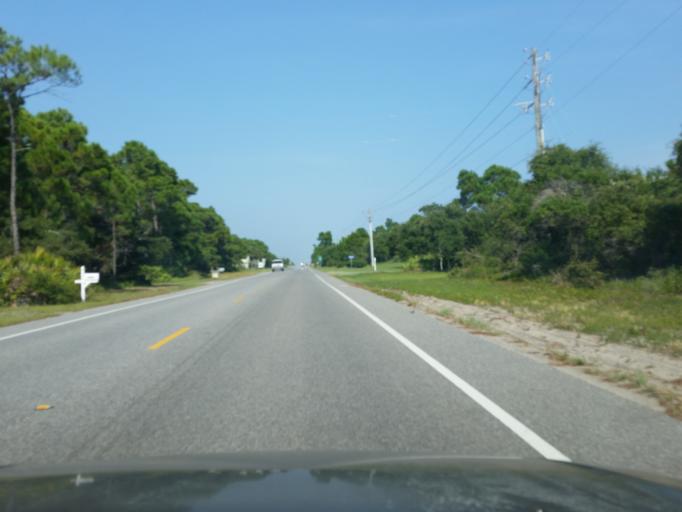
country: US
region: Alabama
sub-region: Mobile County
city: Dauphin Island
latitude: 30.2310
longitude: -87.9967
